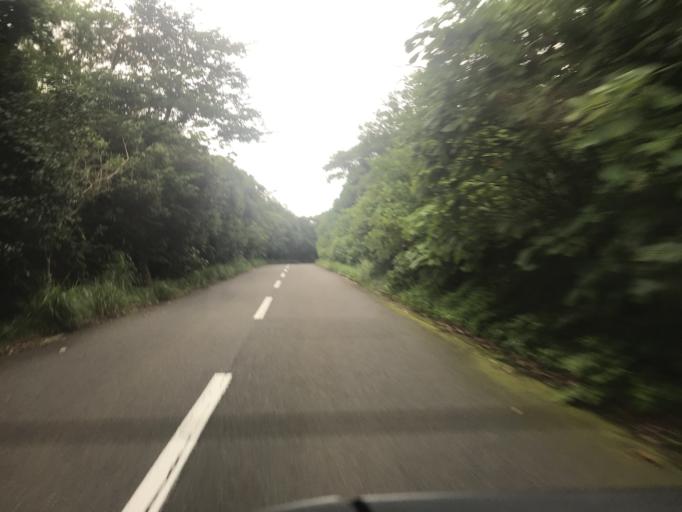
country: JP
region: Shizuoka
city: Ito
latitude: 34.7594
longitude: 139.3998
